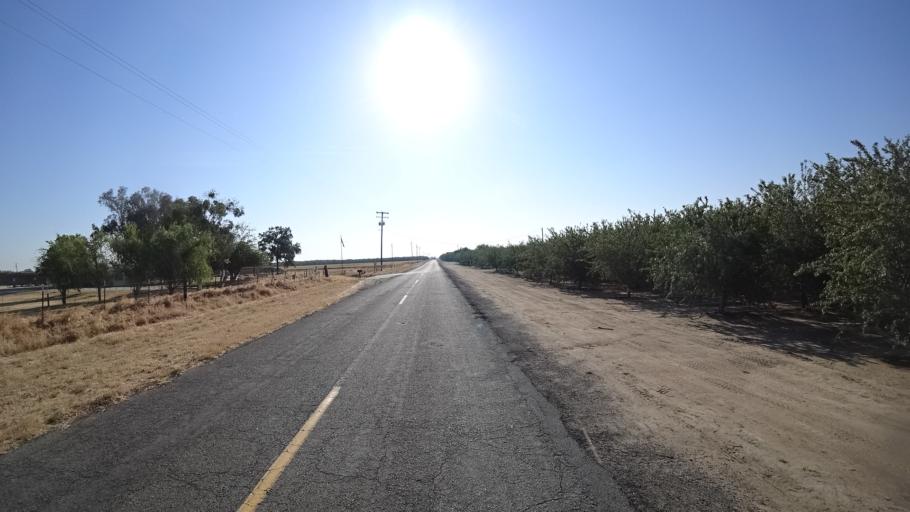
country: US
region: California
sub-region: Fresno County
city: Riverdale
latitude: 36.3765
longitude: -119.8756
